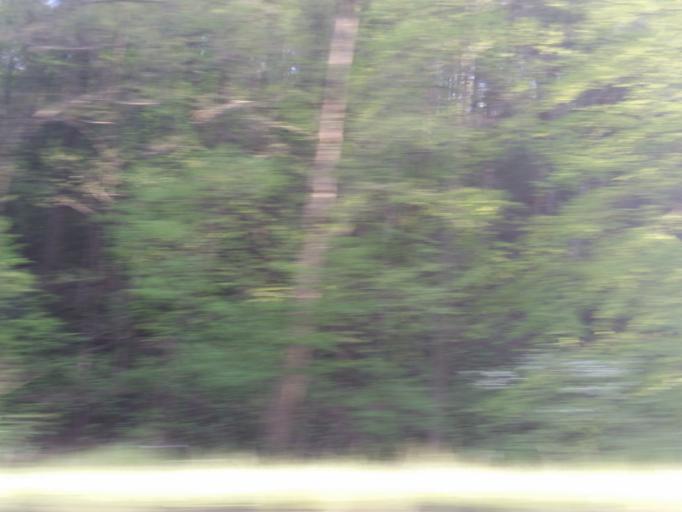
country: US
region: Kentucky
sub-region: Bell County
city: Middlesboro
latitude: 36.6093
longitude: -83.8167
